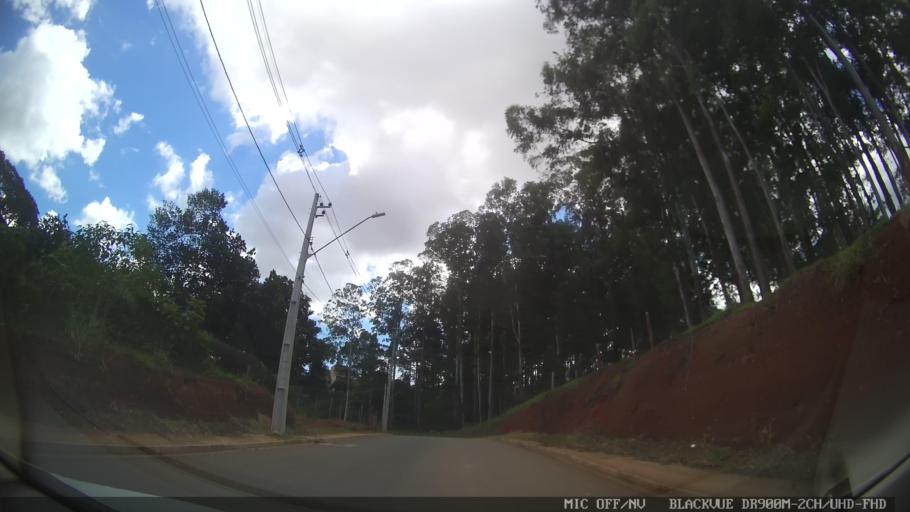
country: BR
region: Minas Gerais
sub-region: Extrema
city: Extrema
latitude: -22.8661
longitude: -46.3335
